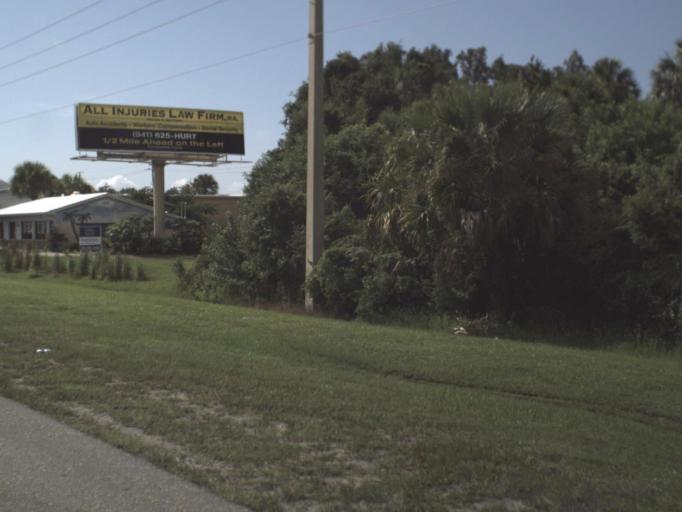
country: US
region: Florida
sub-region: Charlotte County
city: Port Charlotte
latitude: 27.0026
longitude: -82.1273
